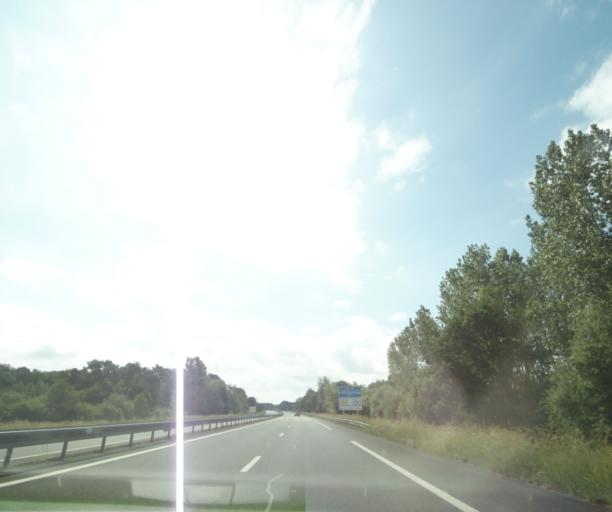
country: FR
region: Pays de la Loire
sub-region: Departement de Maine-et-Loire
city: Brion
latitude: 47.4232
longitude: -0.1412
